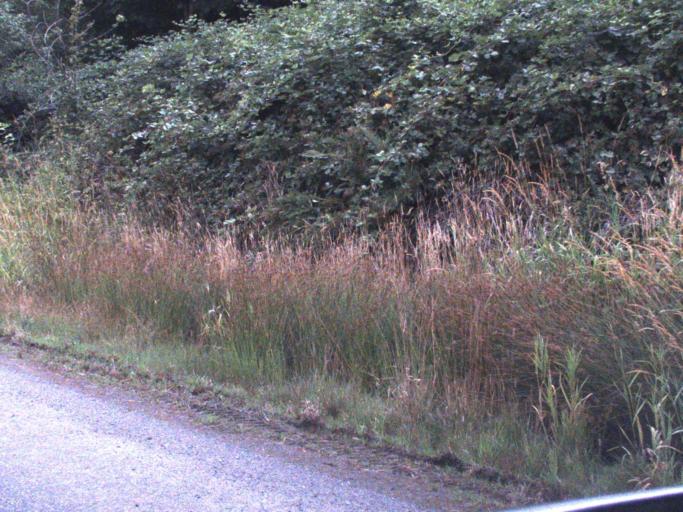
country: US
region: Washington
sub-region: King County
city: Duvall
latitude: 47.7868
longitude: -121.9717
